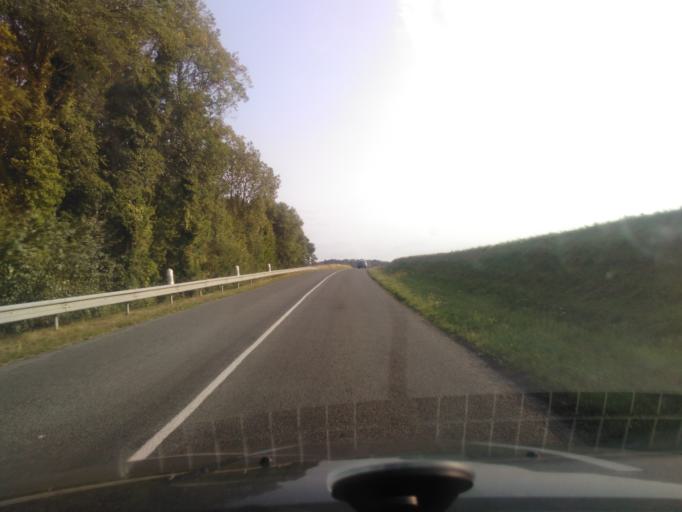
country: FR
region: Picardie
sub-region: Departement de l'Aisne
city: Bruyeres-et-Montberault
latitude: 49.5120
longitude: 3.6751
